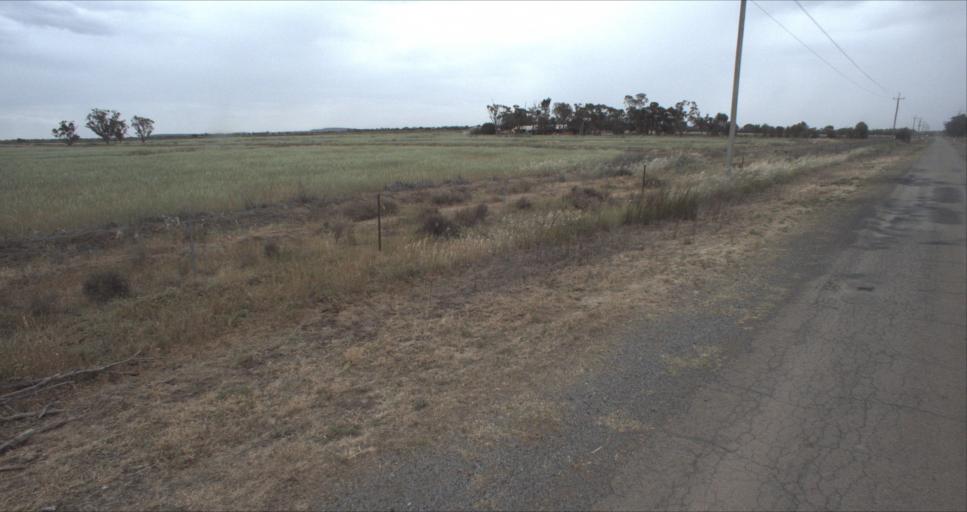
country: AU
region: New South Wales
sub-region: Leeton
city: Leeton
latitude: -34.4105
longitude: 146.3404
